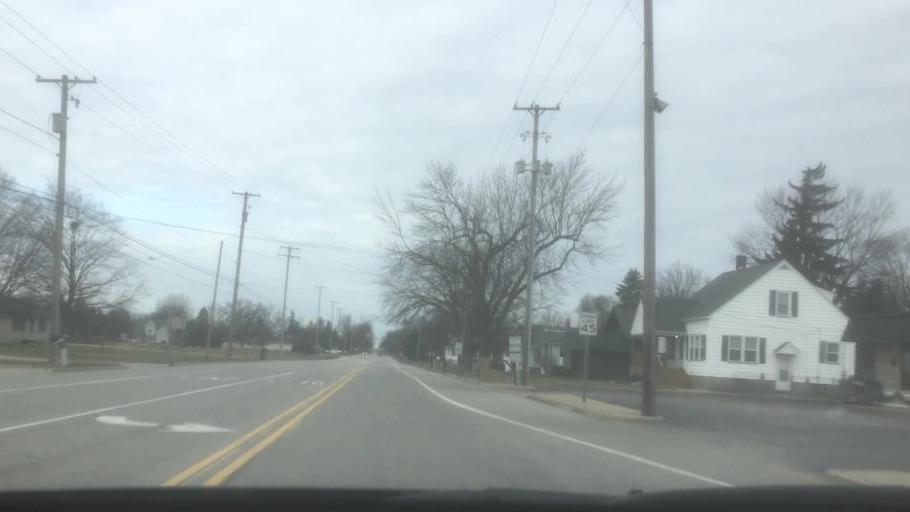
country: US
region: Michigan
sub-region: Bay County
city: Bay City
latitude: 43.6023
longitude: -83.9327
